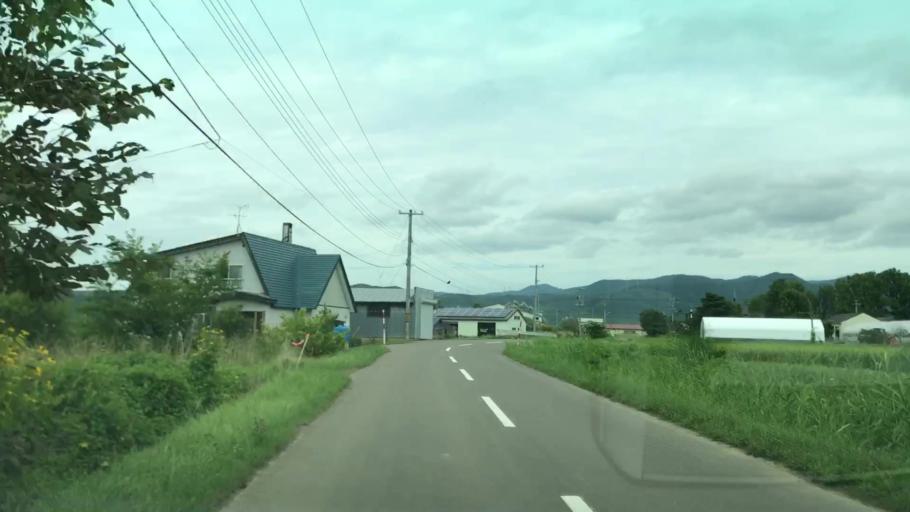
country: JP
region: Hokkaido
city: Iwanai
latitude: 43.0273
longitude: 140.5678
